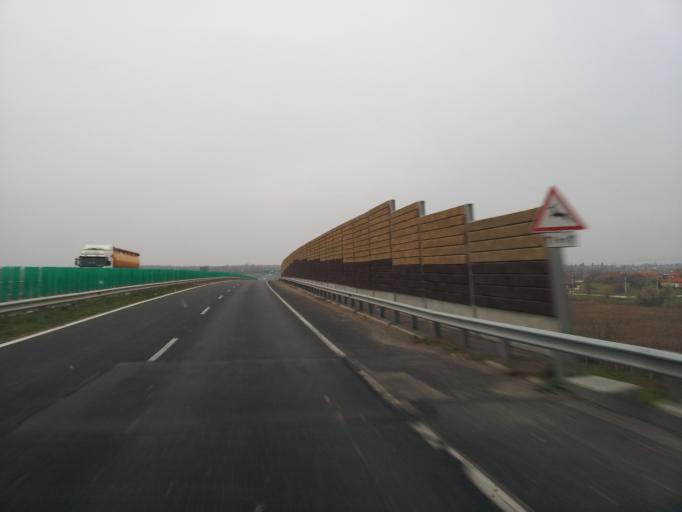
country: HU
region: Fejer
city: Szekesfehervar
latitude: 47.1476
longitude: 18.4075
